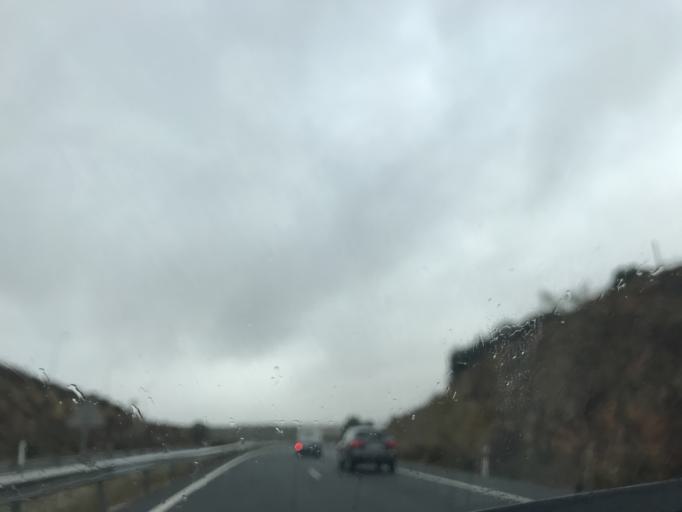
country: ES
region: Andalusia
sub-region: Provincia de Malaga
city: Mollina
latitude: 37.1067
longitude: -4.6539
